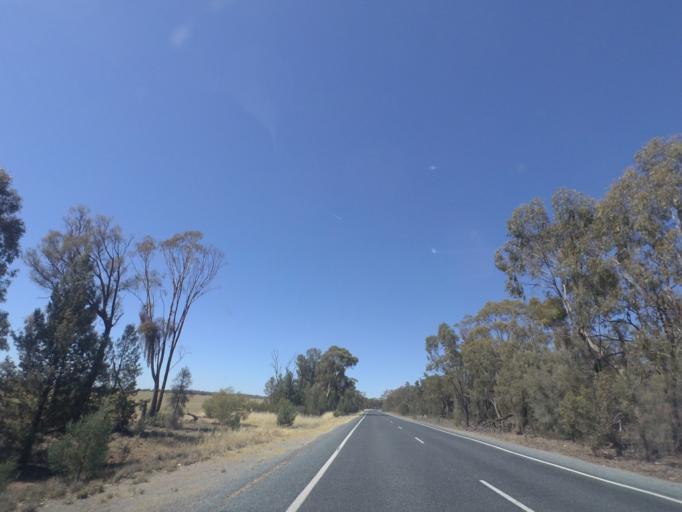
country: AU
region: New South Wales
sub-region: Narrandera
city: Narrandera
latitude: -34.4371
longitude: 146.8420
